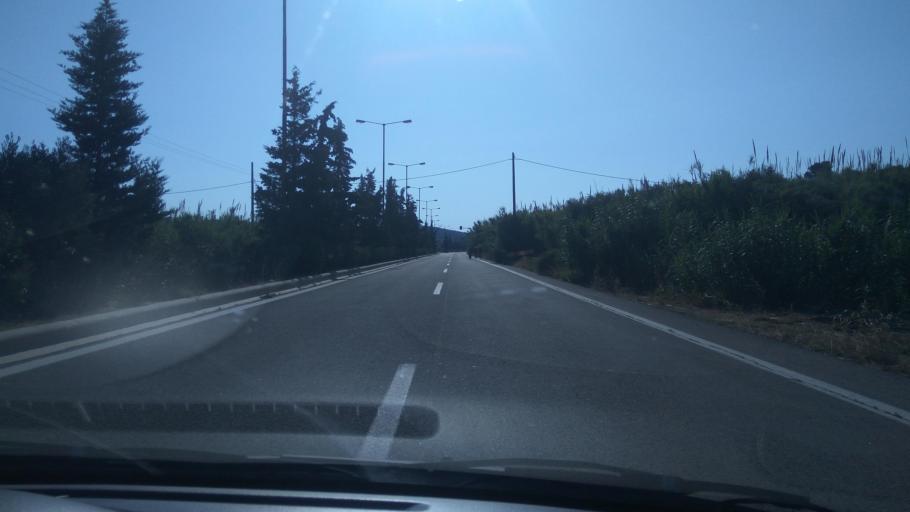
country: GR
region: Attica
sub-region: Nomarchia Anatolikis Attikis
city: Keratea
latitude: 37.8030
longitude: 24.0318
